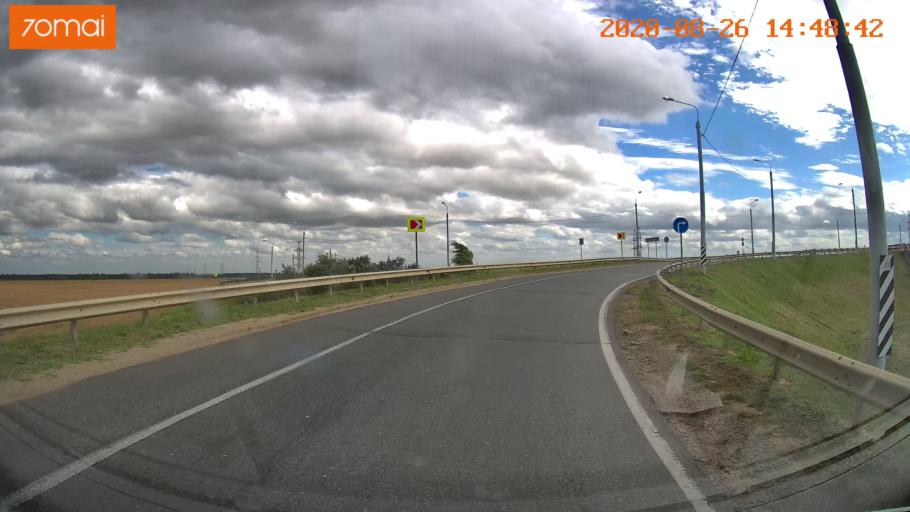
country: RU
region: Rjazan
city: Mikhaylov
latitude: 54.2637
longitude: 39.0064
